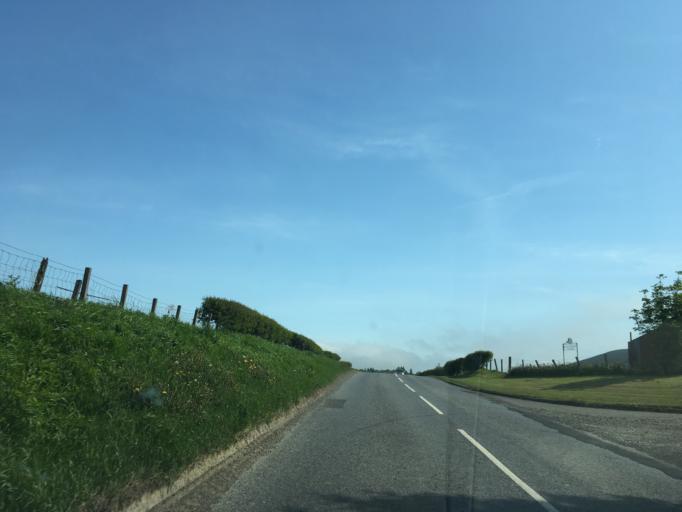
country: GB
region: Scotland
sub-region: The Scottish Borders
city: West Linton
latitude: 55.6741
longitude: -3.4122
